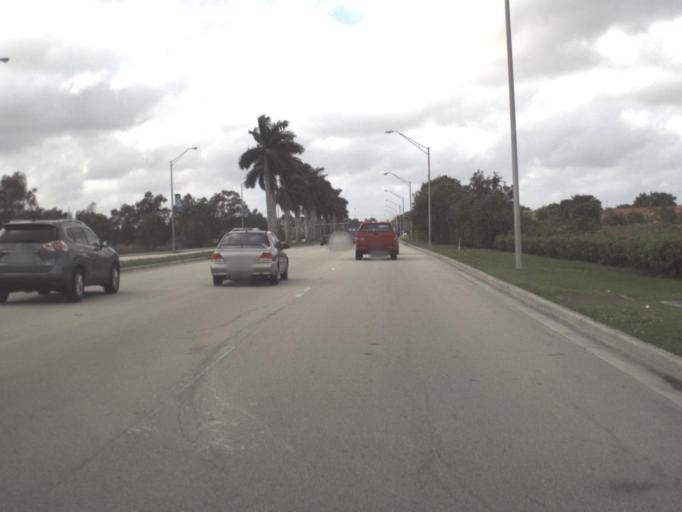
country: US
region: Florida
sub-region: Miami-Dade County
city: Doral
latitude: 25.8118
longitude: -80.3735
